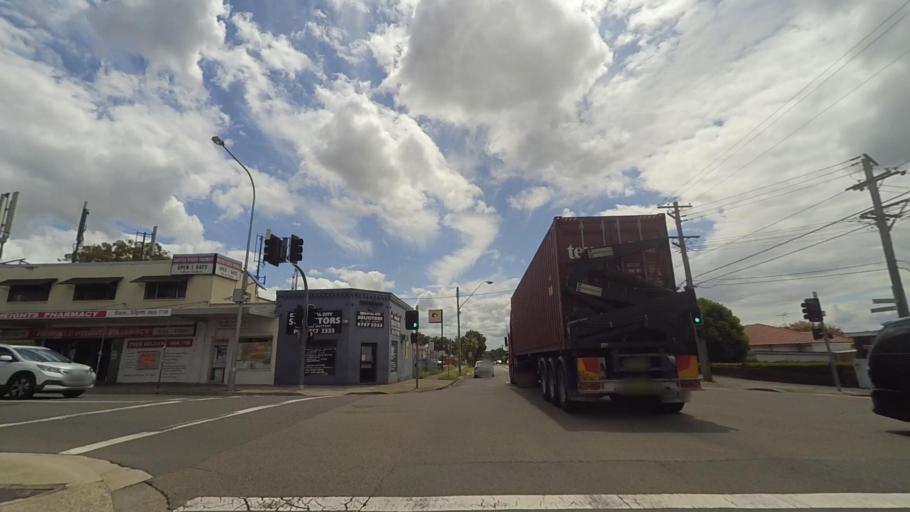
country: AU
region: New South Wales
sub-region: Fairfield
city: Fairfield Heights
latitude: -33.8620
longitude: 150.9390
